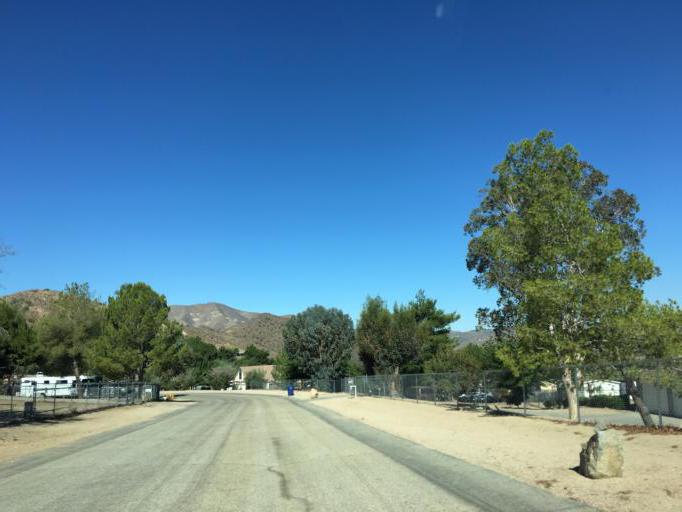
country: US
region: California
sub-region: Los Angeles County
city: Acton
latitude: 34.4628
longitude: -118.1709
